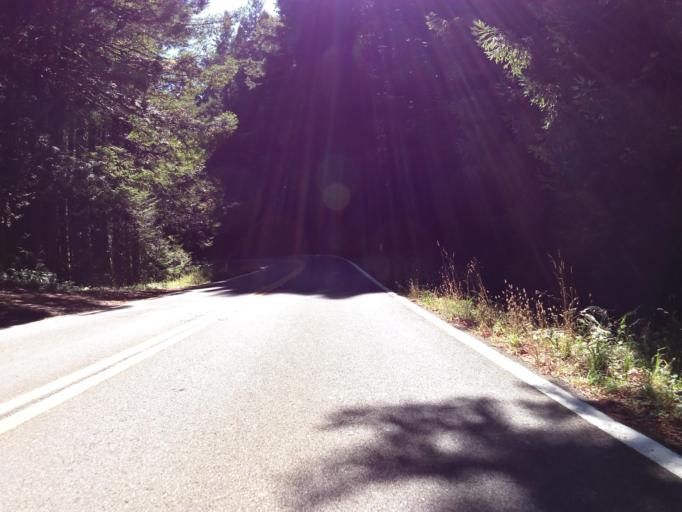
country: US
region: California
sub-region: Mendocino County
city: Fort Bragg
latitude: 39.7232
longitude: -123.8024
